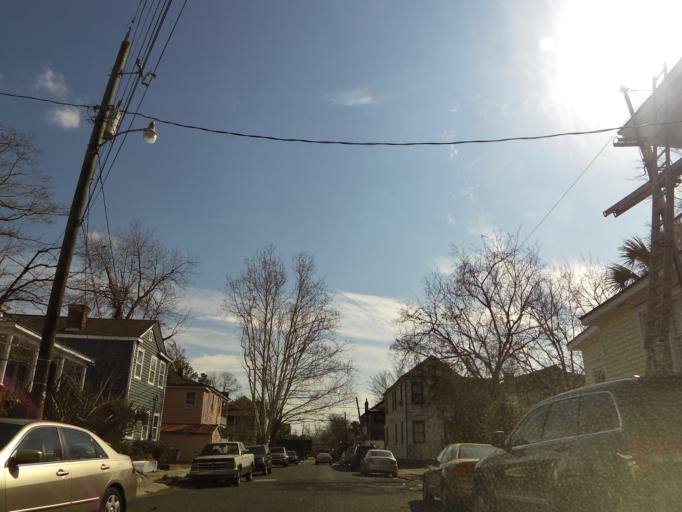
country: US
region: South Carolina
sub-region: Charleston County
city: Charleston
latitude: 32.7959
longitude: -79.9474
